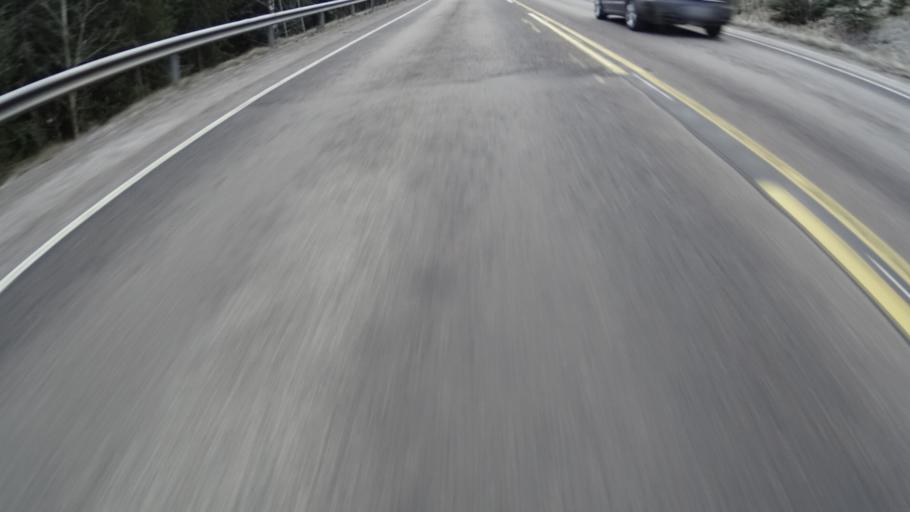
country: FI
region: Uusimaa
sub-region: Helsinki
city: Nurmijaervi
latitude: 60.4109
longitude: 24.7309
